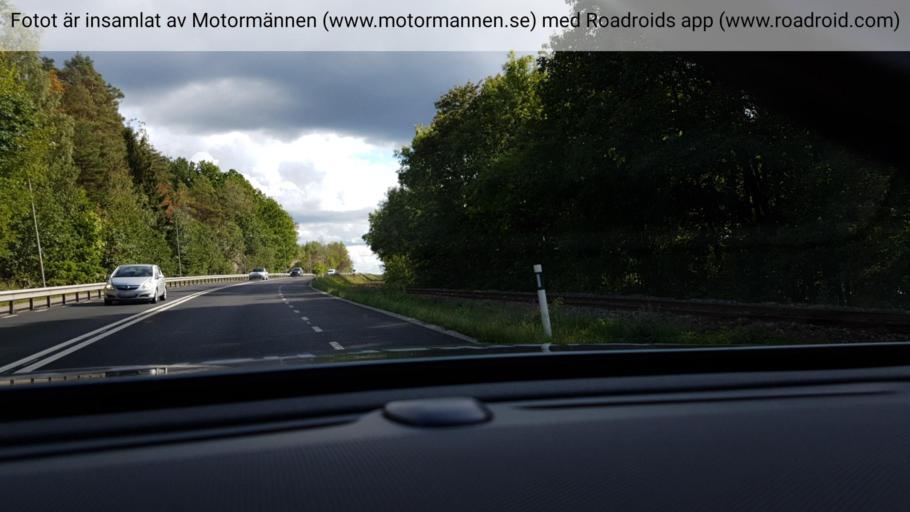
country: SE
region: Vaestra Goetaland
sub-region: Lilla Edets Kommun
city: Lilla Edet
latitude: 58.1023
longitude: 12.1512
